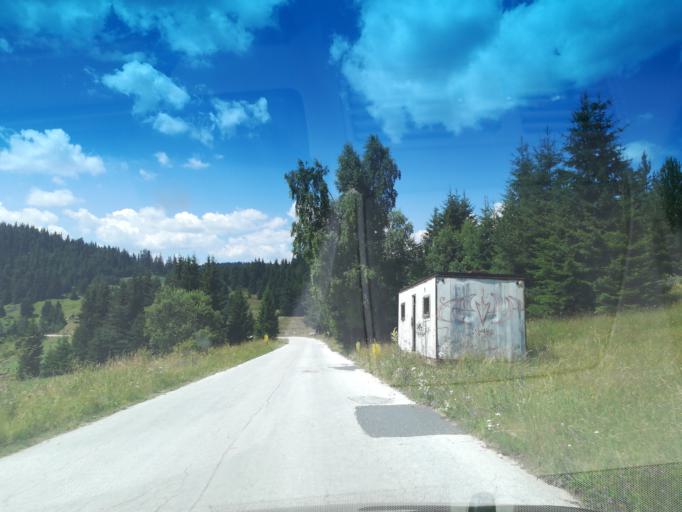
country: BG
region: Smolyan
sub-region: Obshtina Chepelare
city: Chepelare
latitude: 41.6925
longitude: 24.7612
